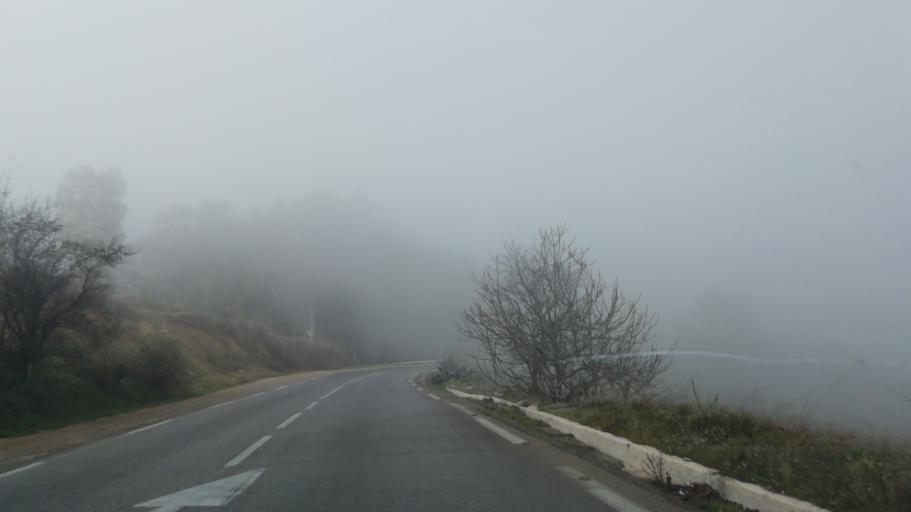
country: DZ
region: Mascara
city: Mascara
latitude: 35.5264
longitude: 0.3393
